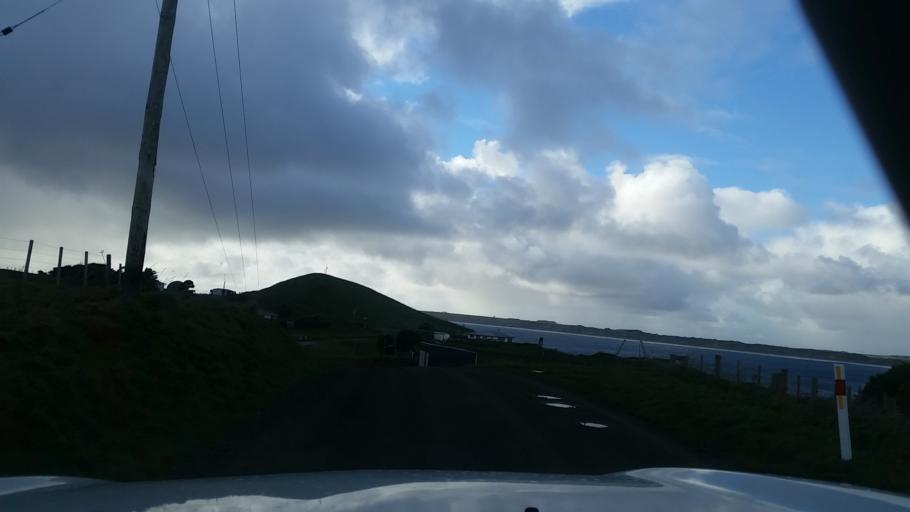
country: NZ
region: Chatham Islands
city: Waitangi
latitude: -43.9487
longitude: -176.5639
